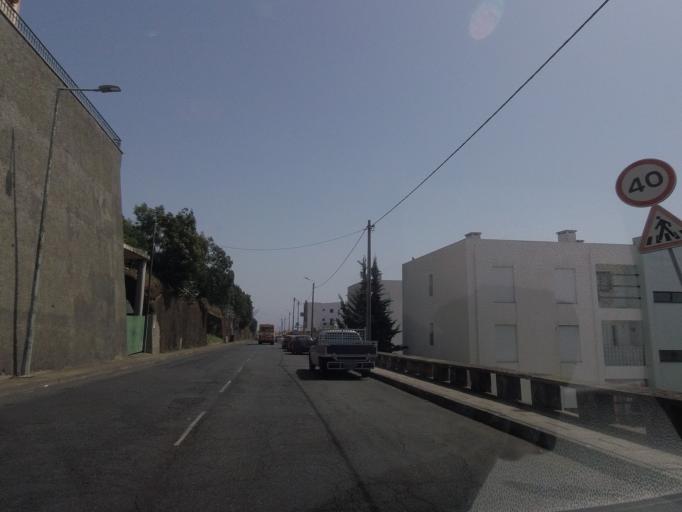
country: PT
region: Madeira
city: Camara de Lobos
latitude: 32.6624
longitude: -16.9479
